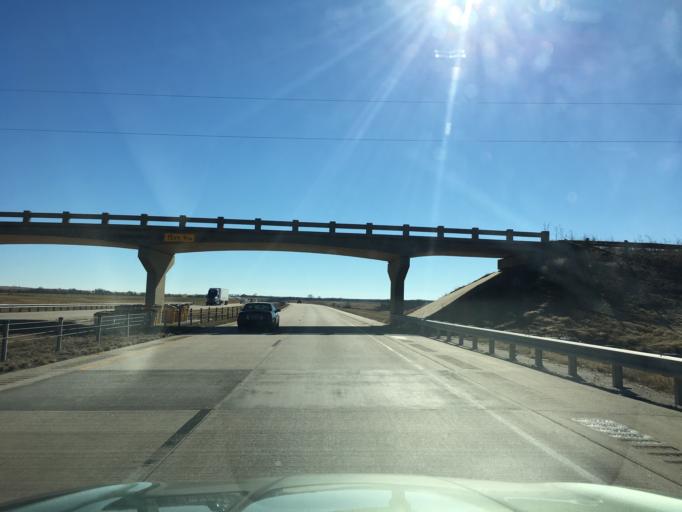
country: US
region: Oklahoma
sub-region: Kay County
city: Tonkawa
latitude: 36.5074
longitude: -97.3367
